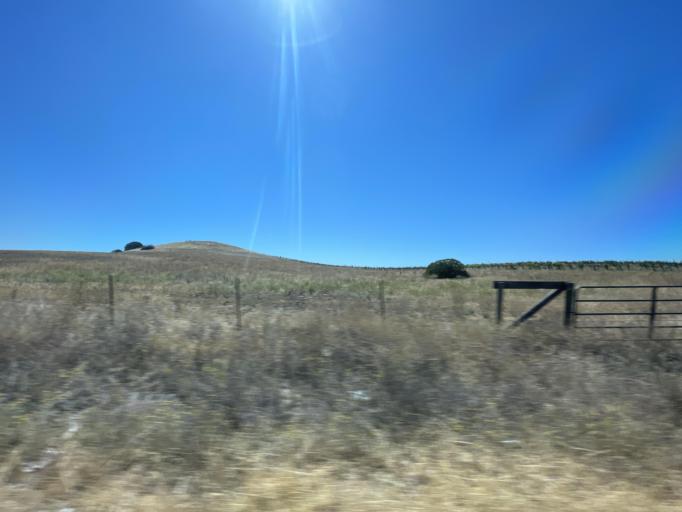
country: US
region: California
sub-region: San Luis Obispo County
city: Paso Robles
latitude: 35.6353
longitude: -120.5996
